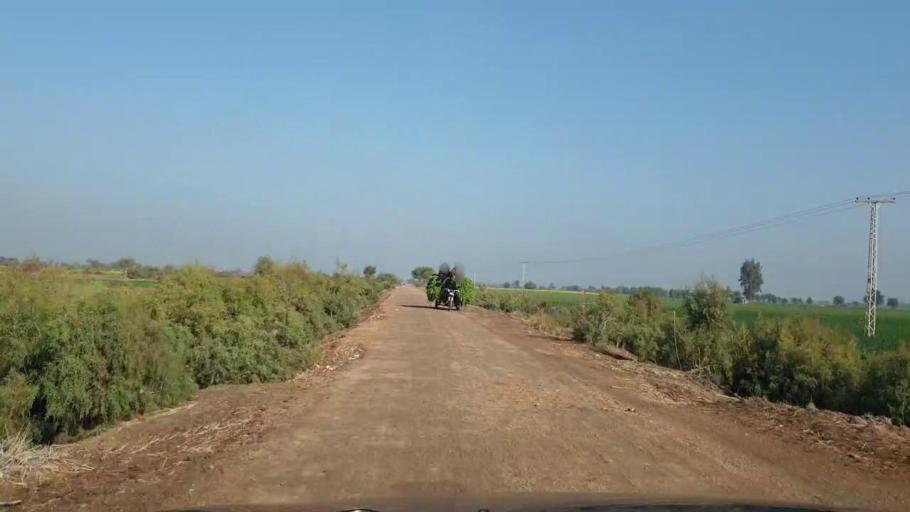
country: PK
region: Sindh
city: Sinjhoro
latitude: 26.0502
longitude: 68.7885
